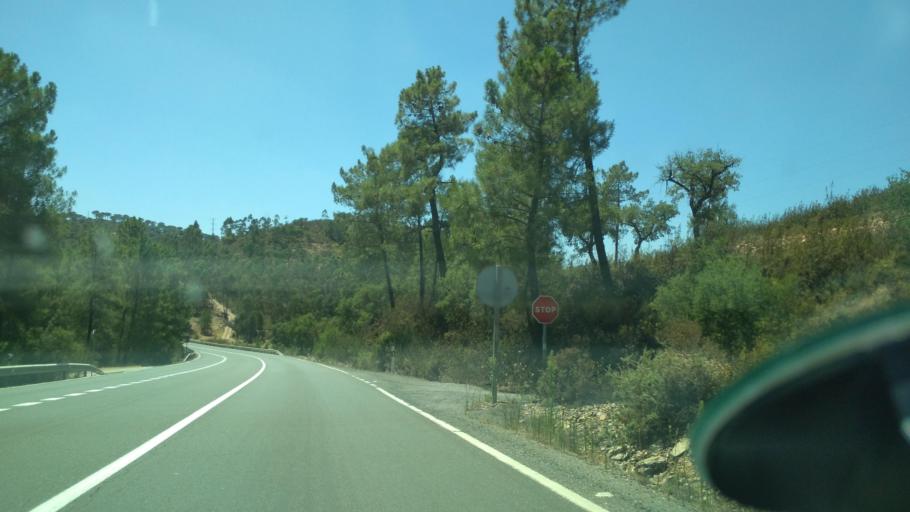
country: ES
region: Andalusia
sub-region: Provincia de Huelva
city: Campofrio
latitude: 37.7560
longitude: -6.5854
